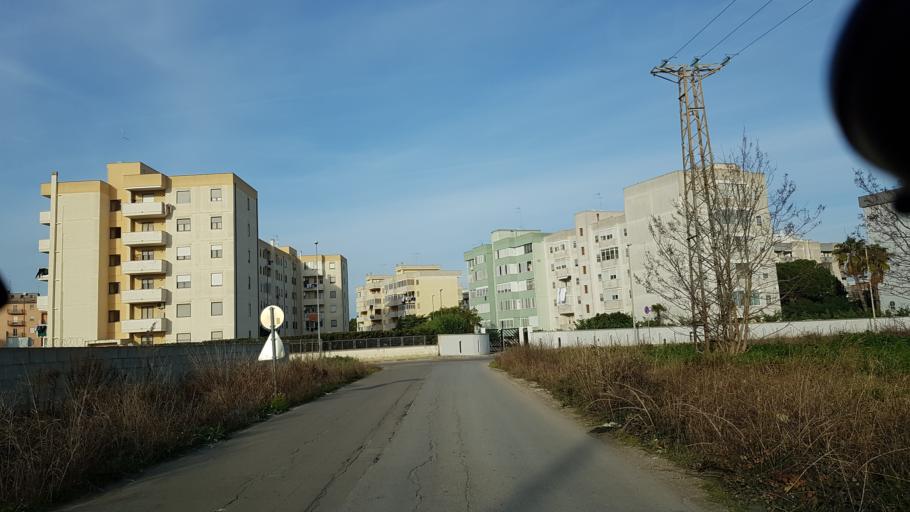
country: IT
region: Apulia
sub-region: Provincia di Brindisi
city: Brindisi
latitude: 40.6166
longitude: 17.9177
